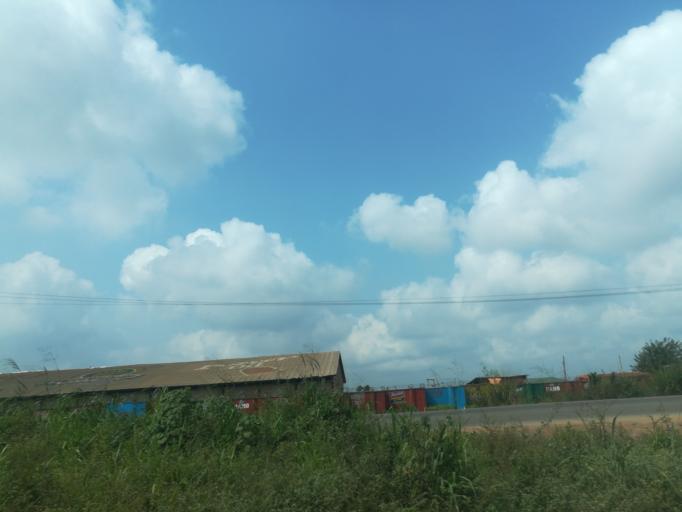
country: NG
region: Oyo
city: Ibadan
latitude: 7.4247
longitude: 3.9357
